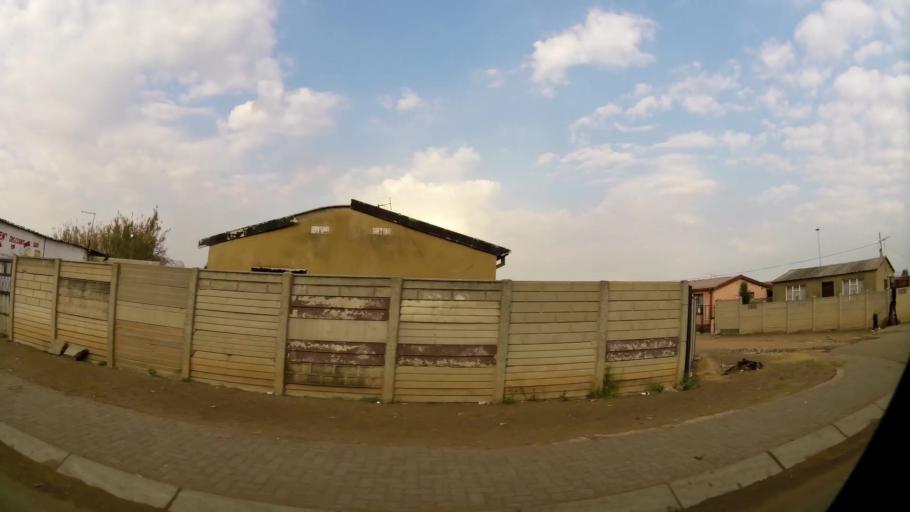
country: ZA
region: Gauteng
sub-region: Sedibeng District Municipality
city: Vanderbijlpark
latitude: -26.6945
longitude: 27.8745
